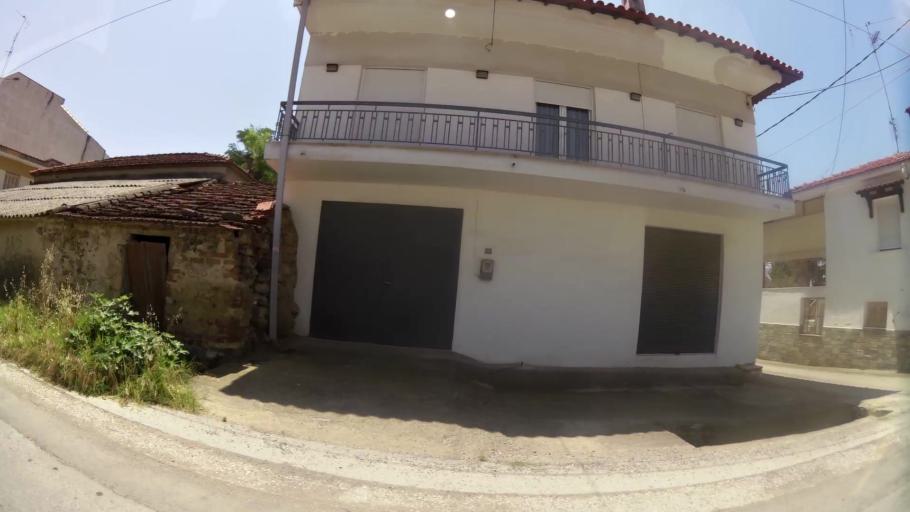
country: GR
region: Central Macedonia
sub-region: Nomos Thessalonikis
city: Epanomi
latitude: 40.4308
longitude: 22.9250
